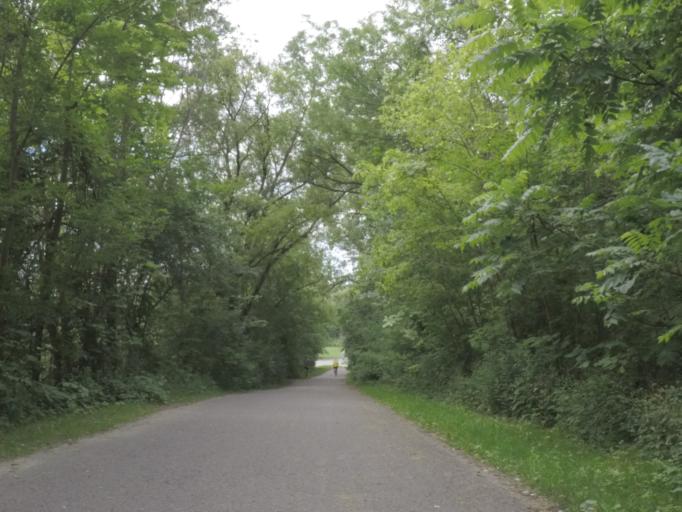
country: CA
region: Ontario
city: Etobicoke
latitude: 43.6448
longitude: -79.4927
